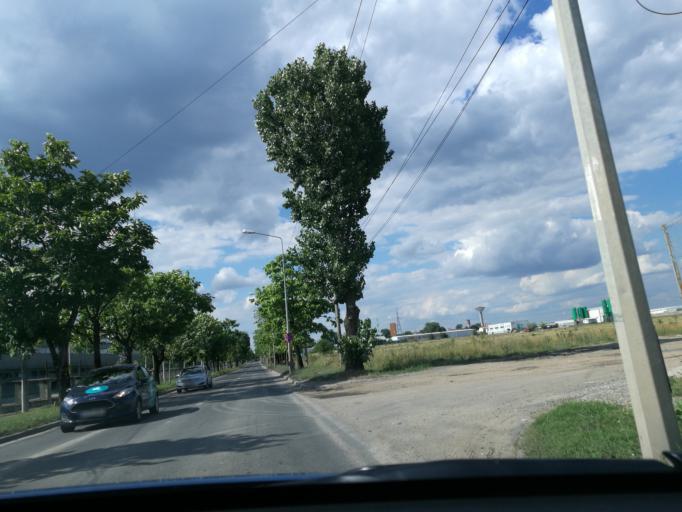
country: RO
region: Ilfov
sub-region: Comuna Glina
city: Catelu
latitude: 44.4125
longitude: 26.2181
